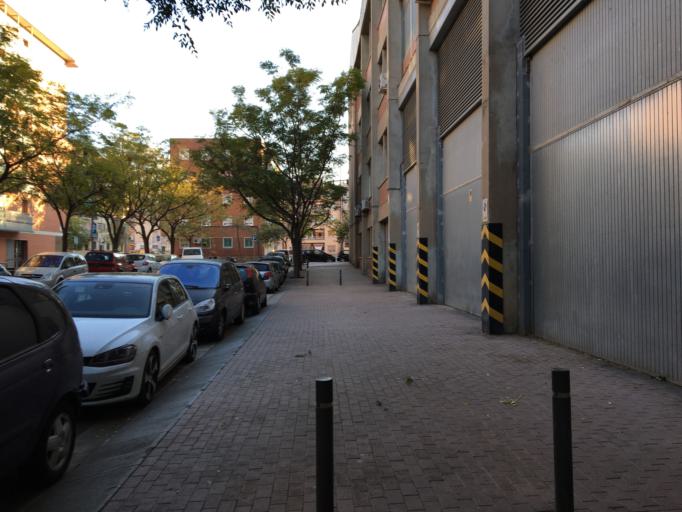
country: ES
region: Catalonia
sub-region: Provincia de Barcelona
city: Sant Andreu de Palomar
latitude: 41.4365
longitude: 2.2032
